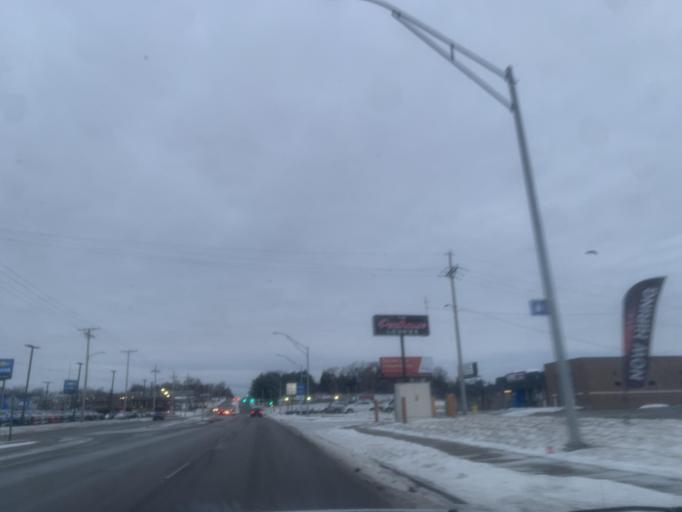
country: US
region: Nebraska
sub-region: Douglas County
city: Ralston
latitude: 41.2148
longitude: -96.0432
